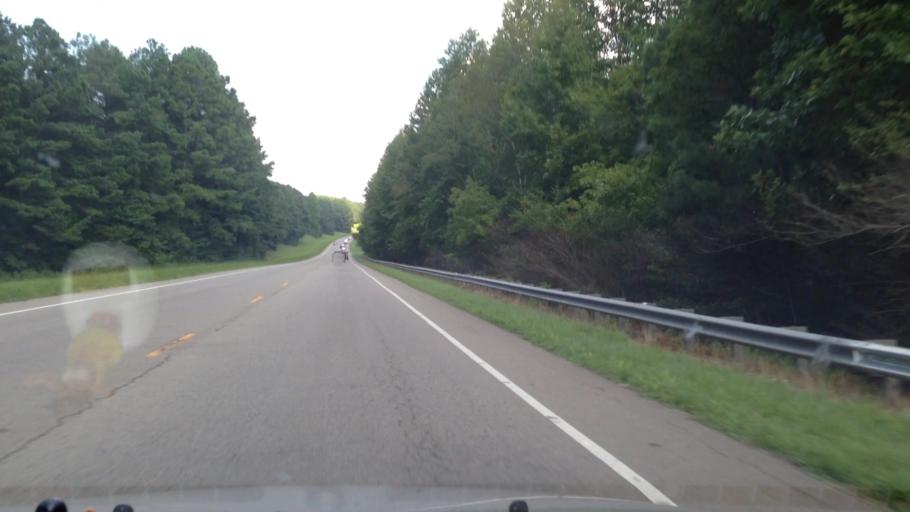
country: US
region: North Carolina
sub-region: Lee County
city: Broadway
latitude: 35.4397
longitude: -79.0831
